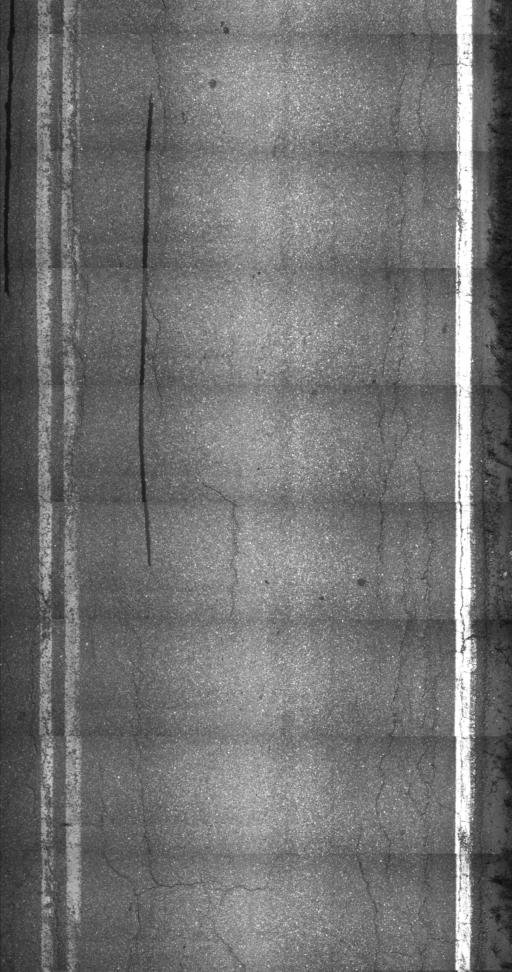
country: US
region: Vermont
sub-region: Windsor County
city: Chester
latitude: 43.3945
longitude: -72.5931
